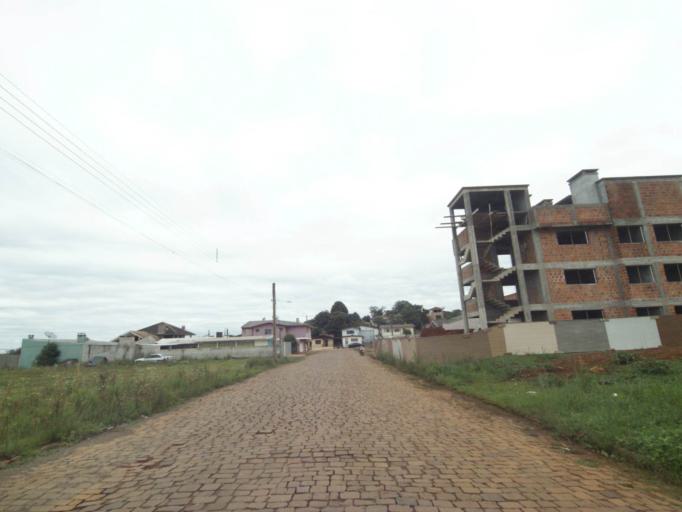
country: BR
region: Rio Grande do Sul
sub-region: Lagoa Vermelha
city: Lagoa Vermelha
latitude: -28.2150
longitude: -51.5325
